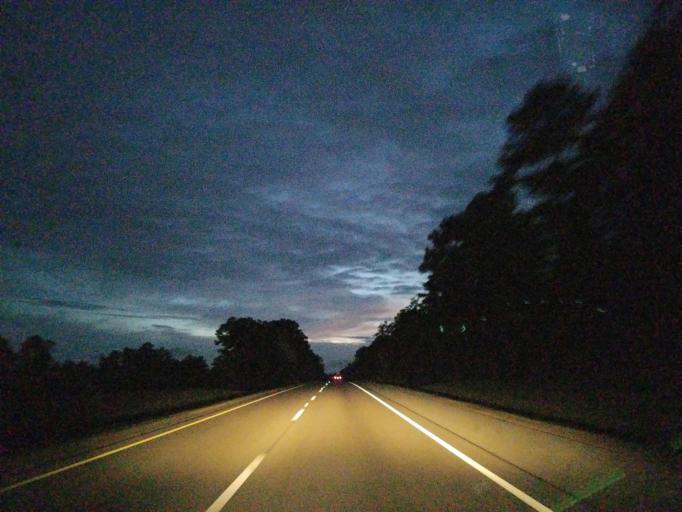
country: US
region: Mississippi
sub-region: Jones County
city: Sharon
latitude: 31.7351
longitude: -89.0930
